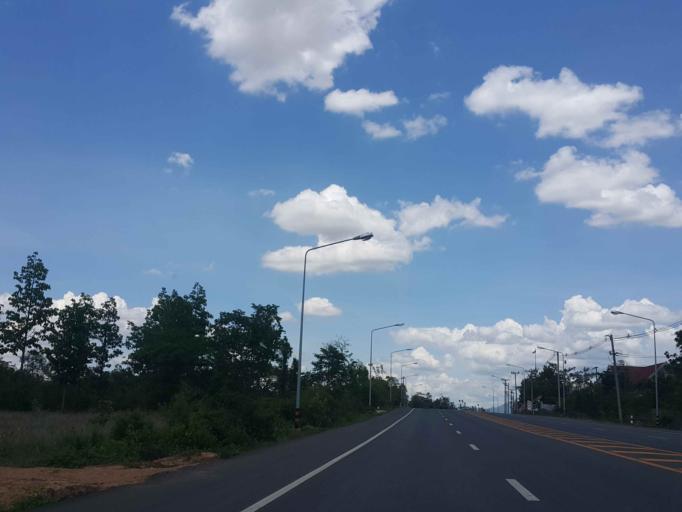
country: TH
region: Phrae
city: Nong Muang Khai
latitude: 18.2024
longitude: 100.2177
